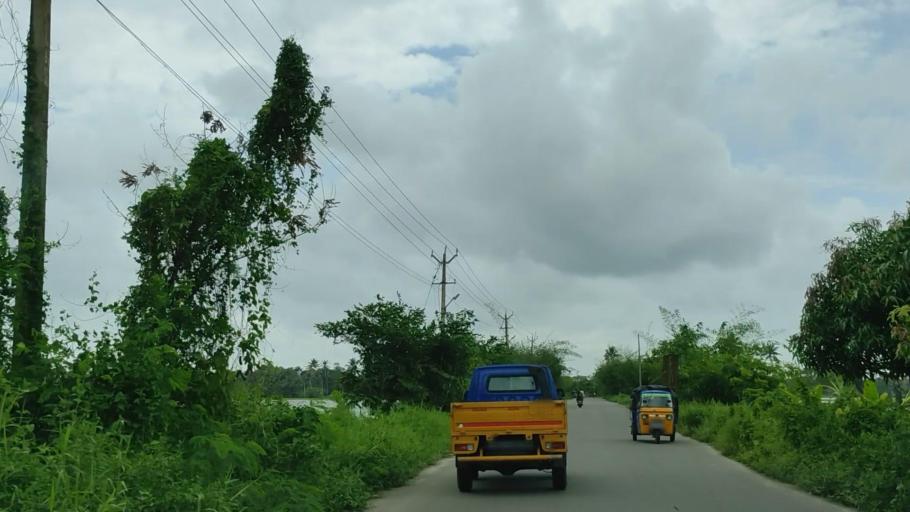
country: IN
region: Kerala
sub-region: Kottayam
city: Kottayam
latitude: 9.5669
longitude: 76.5055
